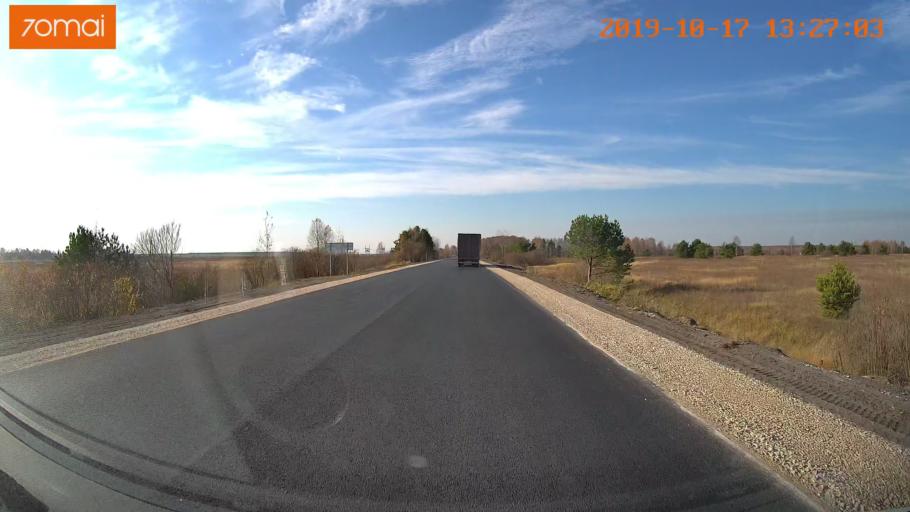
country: RU
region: Rjazan
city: Gus'-Zheleznyy
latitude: 55.1120
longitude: 40.9045
